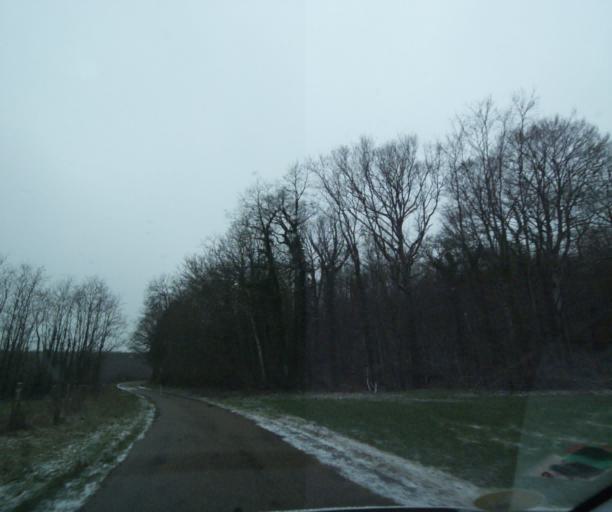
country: FR
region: Champagne-Ardenne
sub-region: Departement de la Haute-Marne
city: Wassy
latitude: 48.4652
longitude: 5.0126
